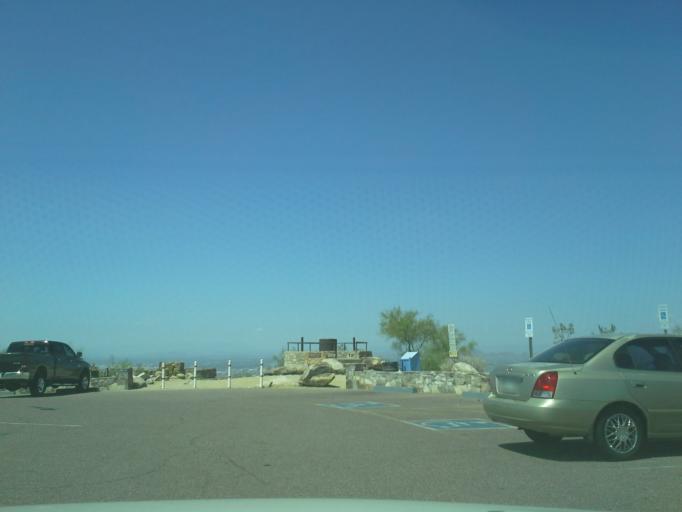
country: US
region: Arizona
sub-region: Maricopa County
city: Guadalupe
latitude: 33.3448
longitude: -112.0584
